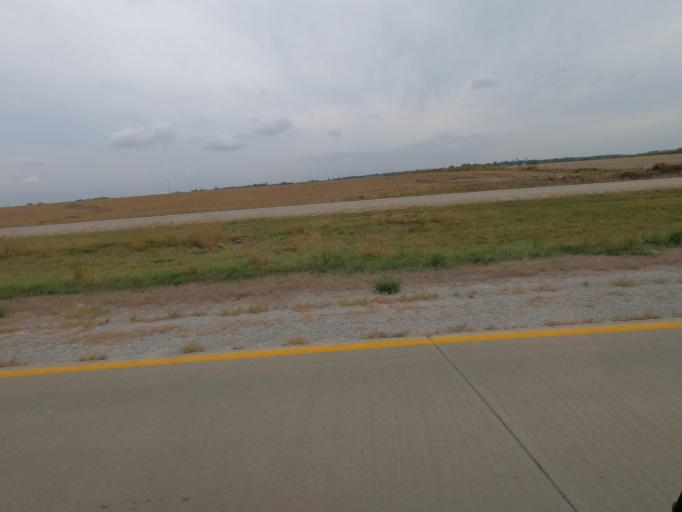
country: US
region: Iowa
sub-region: Jasper County
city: Monroe
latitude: 41.5304
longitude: -93.1304
